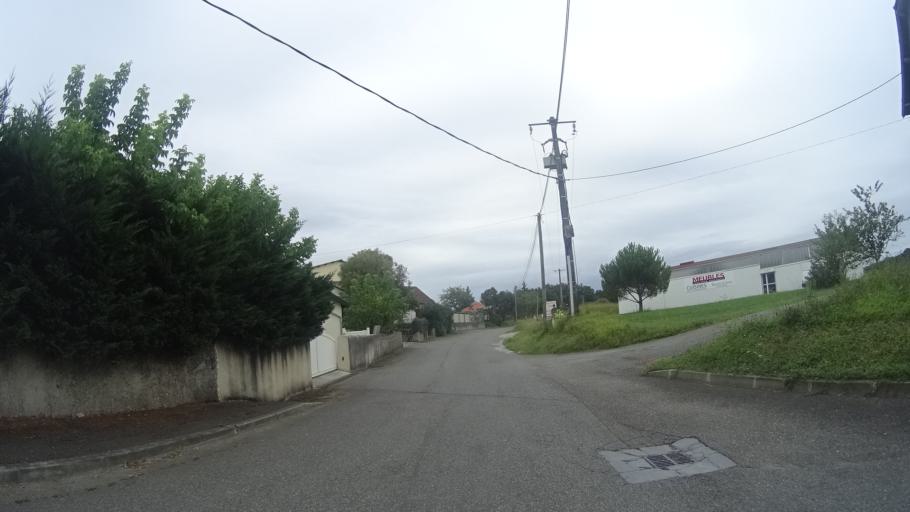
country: FR
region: Aquitaine
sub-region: Departement des Pyrenees-Atlantiques
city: Orthez
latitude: 43.4746
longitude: -0.7295
